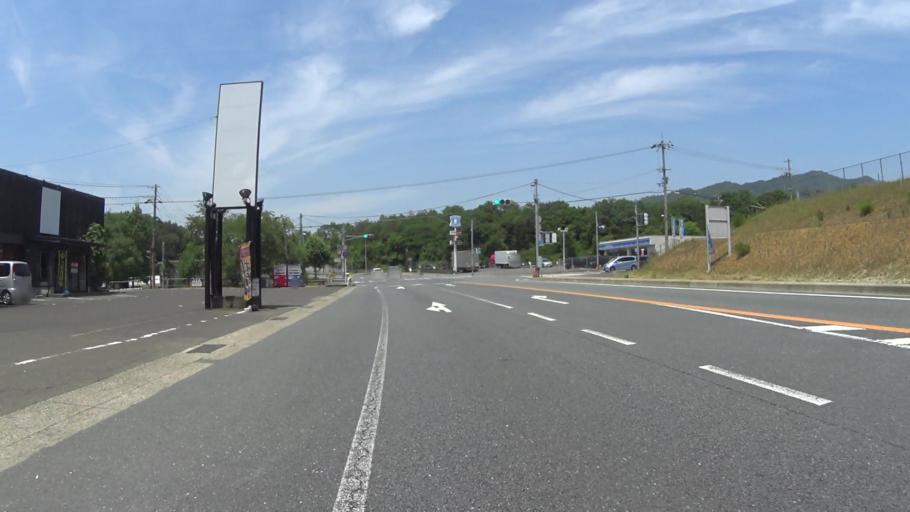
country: JP
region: Kyoto
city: Fukuchiyama
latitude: 35.2728
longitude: 135.1833
